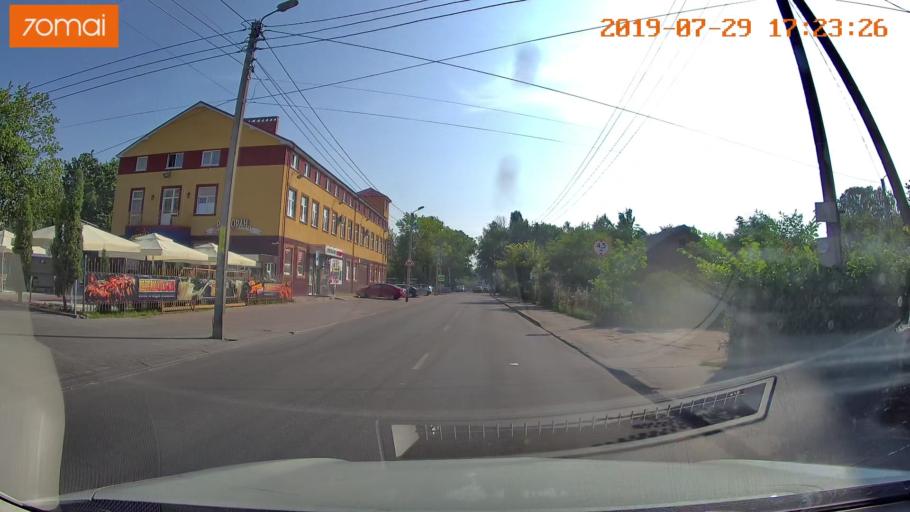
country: RU
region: Kaliningrad
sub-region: Gorod Kaliningrad
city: Kaliningrad
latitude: 54.7657
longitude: 20.4451
